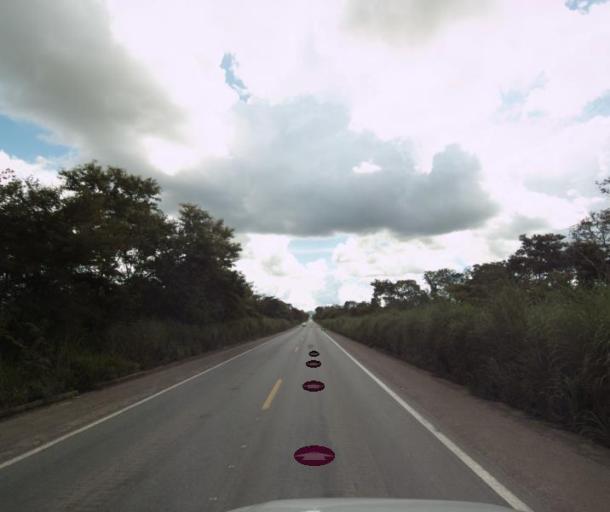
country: BR
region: Goias
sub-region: Porangatu
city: Porangatu
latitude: -13.5542
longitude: -49.0784
